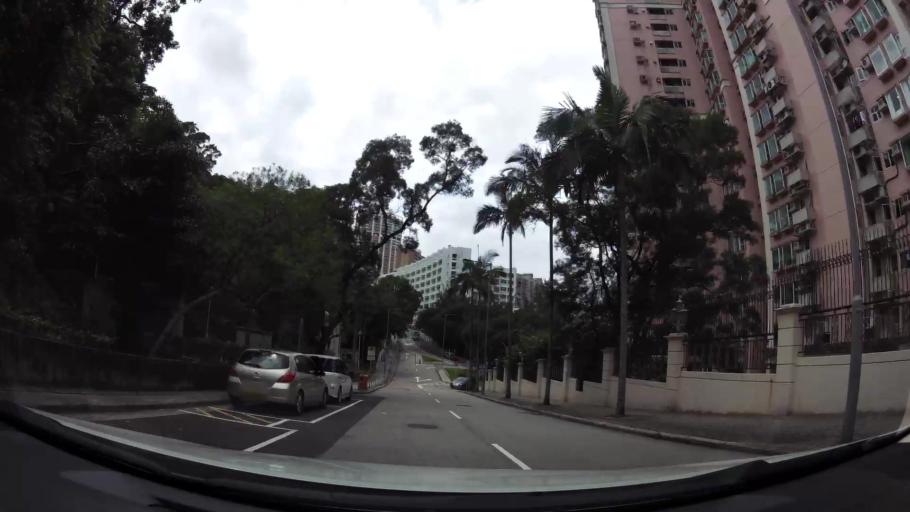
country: HK
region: Wanchai
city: Wan Chai
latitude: 22.2876
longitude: 114.2029
